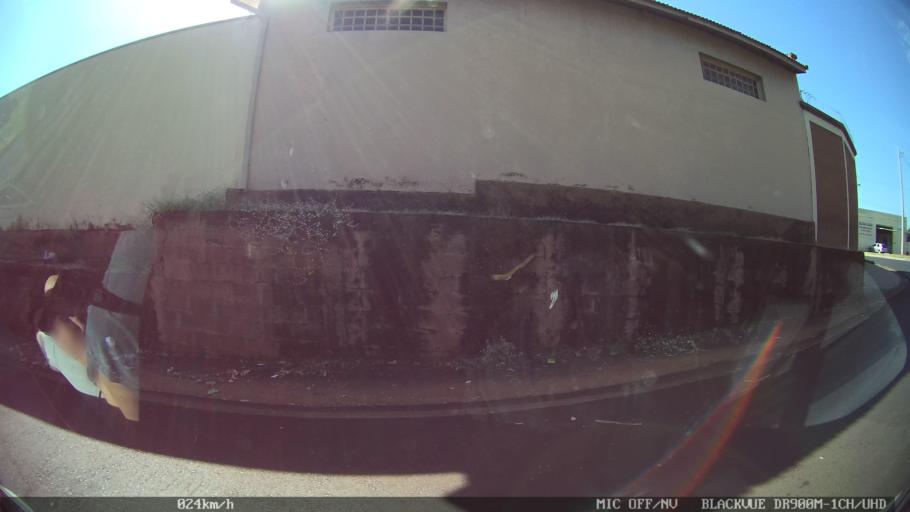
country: BR
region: Sao Paulo
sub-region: Batatais
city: Batatais
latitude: -20.8819
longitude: -47.6026
